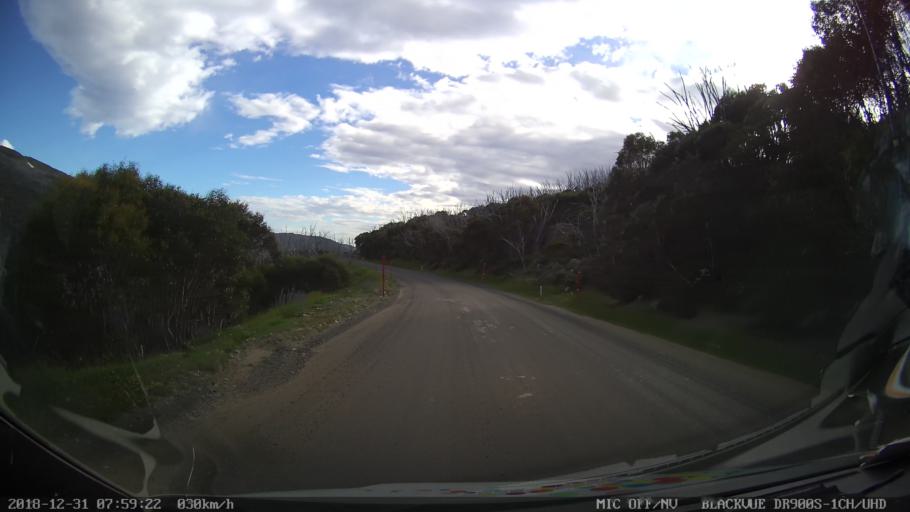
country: AU
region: New South Wales
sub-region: Snowy River
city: Jindabyne
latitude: -36.3717
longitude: 148.3849
